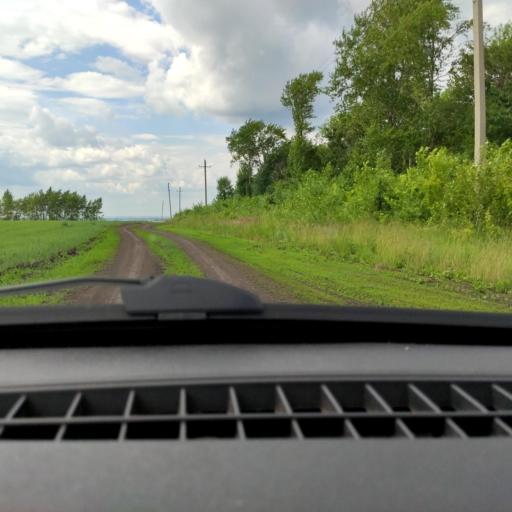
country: RU
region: Bashkortostan
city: Kabakovo
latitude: 54.5248
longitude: 56.0634
